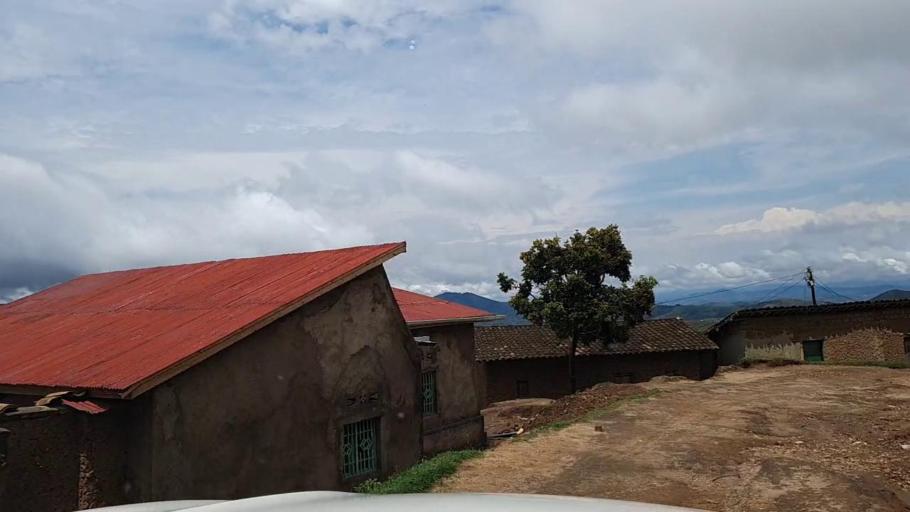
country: RW
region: Southern Province
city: Gikongoro
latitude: -2.3427
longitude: 29.5089
